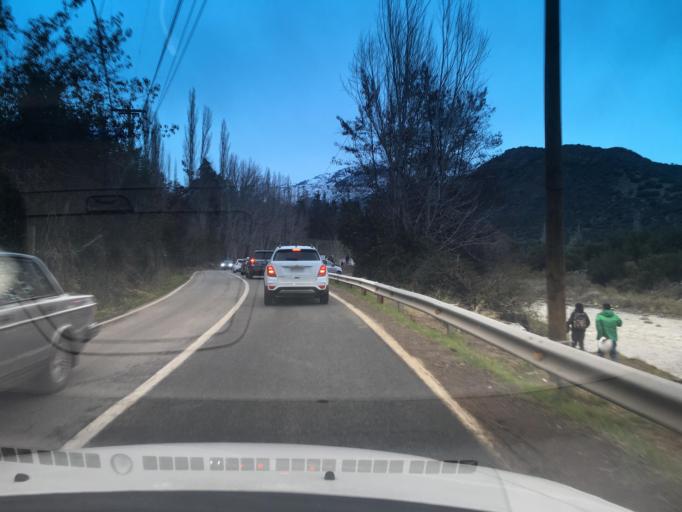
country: CL
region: Santiago Metropolitan
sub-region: Provincia de Cordillera
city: Puente Alto
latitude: -33.6805
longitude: -70.3389
